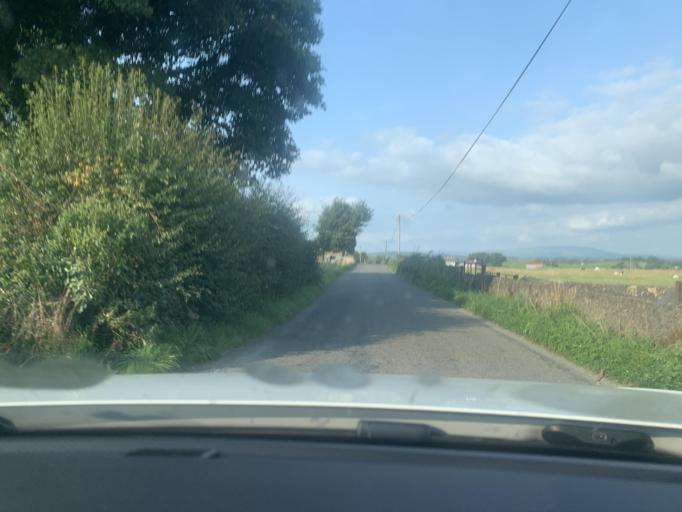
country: IE
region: Connaught
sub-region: Roscommon
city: Boyle
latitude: 53.9631
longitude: -8.2011
